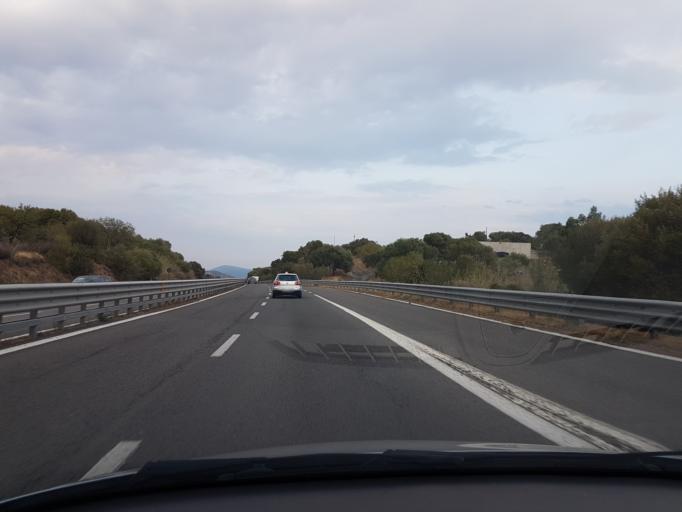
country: IT
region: Sardinia
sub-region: Provincia di Nuoro
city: Orune
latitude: 40.3696
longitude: 9.3897
